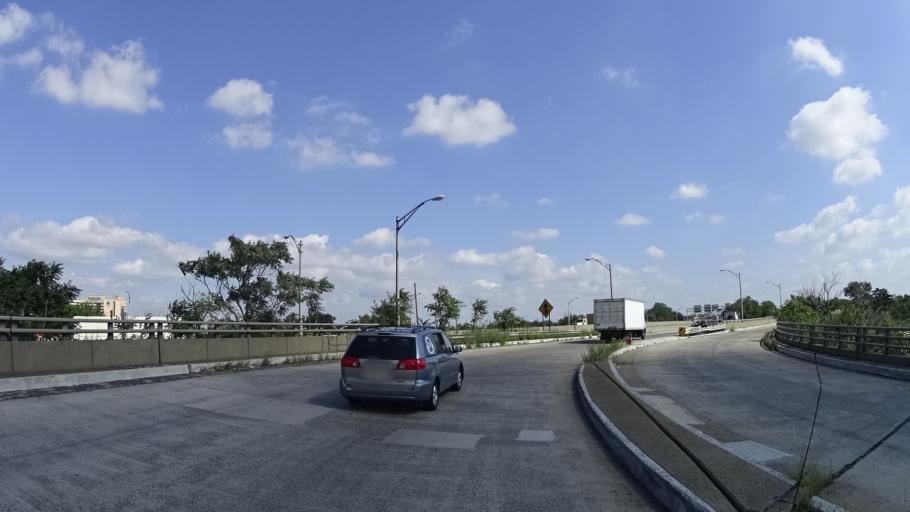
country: US
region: New Jersey
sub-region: Essex County
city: Newark
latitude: 40.7087
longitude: -74.1613
